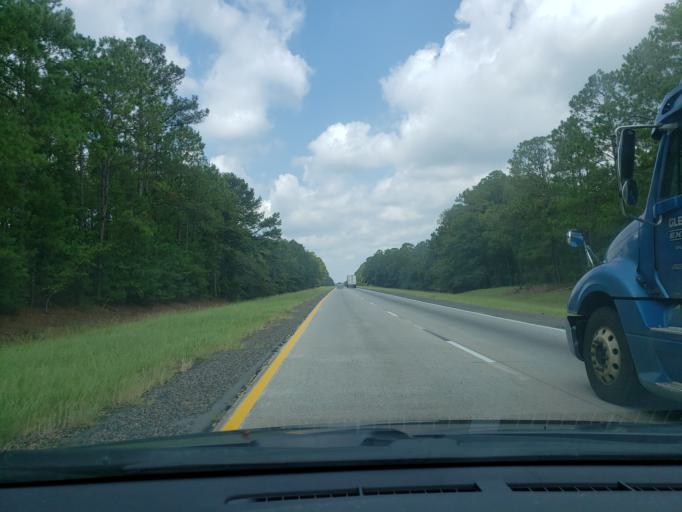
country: US
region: Georgia
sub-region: Treutlen County
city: Soperton
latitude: 32.4268
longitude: -82.5509
